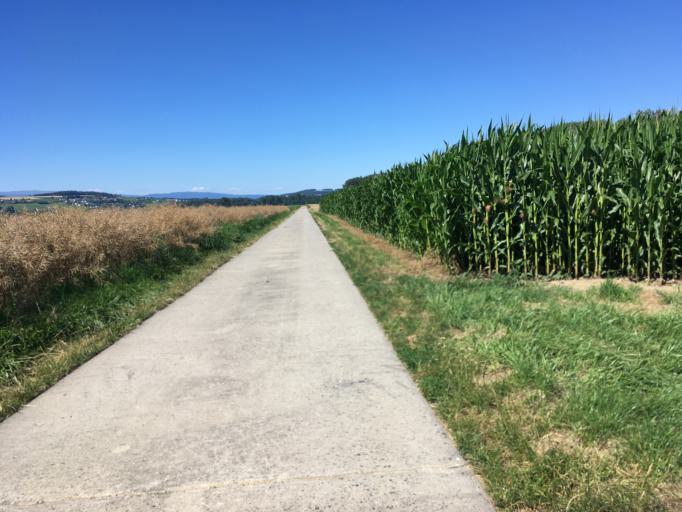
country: CH
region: Vaud
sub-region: Broye-Vully District
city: Avenches
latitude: 46.8922
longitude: 7.0210
